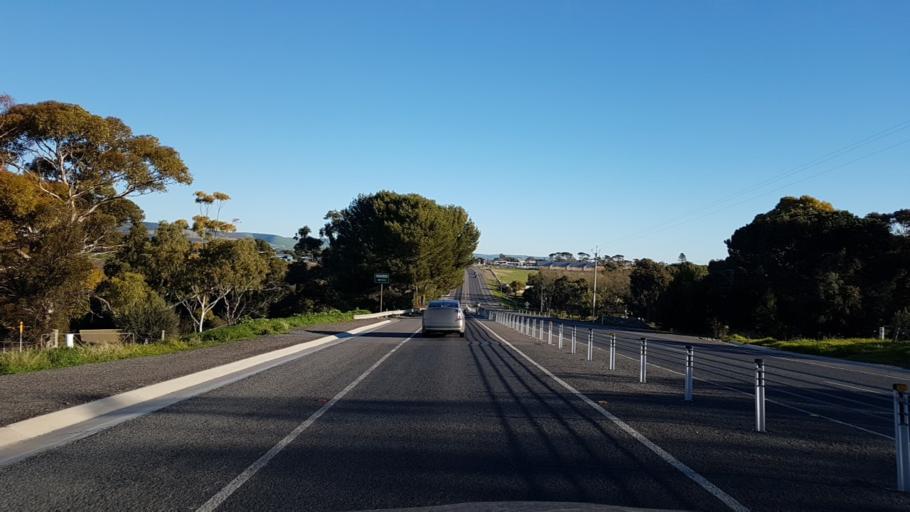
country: AU
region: South Australia
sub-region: Onkaparinga
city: Aldinga
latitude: -35.2621
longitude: 138.4891
